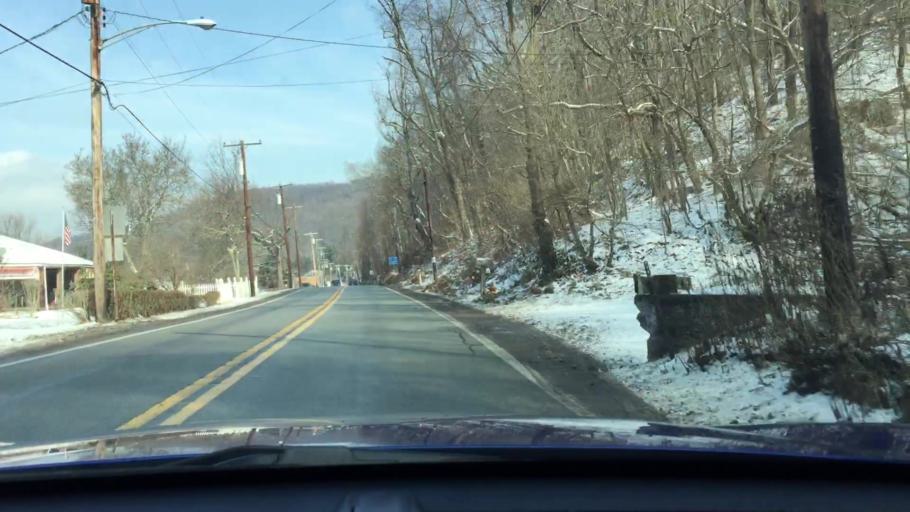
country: US
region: Pennsylvania
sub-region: Allegheny County
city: Clairton
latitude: 40.2841
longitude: -79.8699
